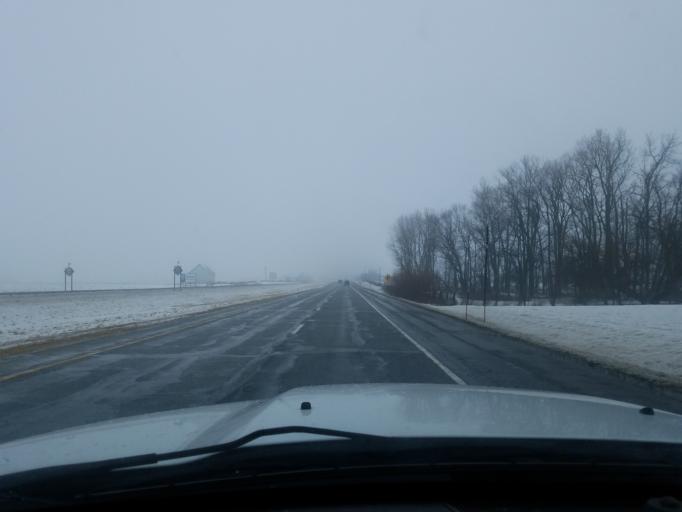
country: US
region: Indiana
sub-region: Tipton County
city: Tipton
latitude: 40.2927
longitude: -86.1268
